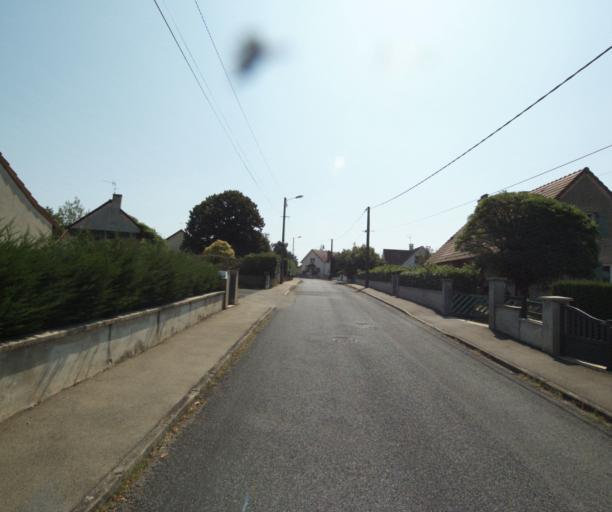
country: FR
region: Bourgogne
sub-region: Departement de Saone-et-Loire
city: Gueugnon
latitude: 46.5978
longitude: 4.0747
